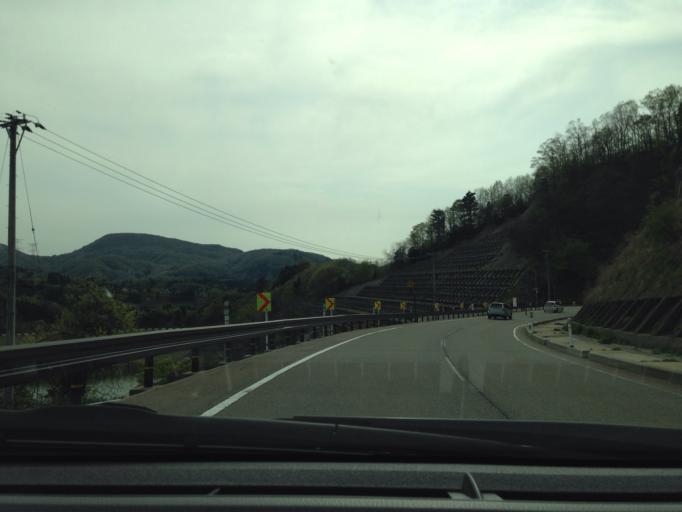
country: JP
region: Toyama
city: Fukumitsu
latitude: 36.5632
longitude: 136.7801
